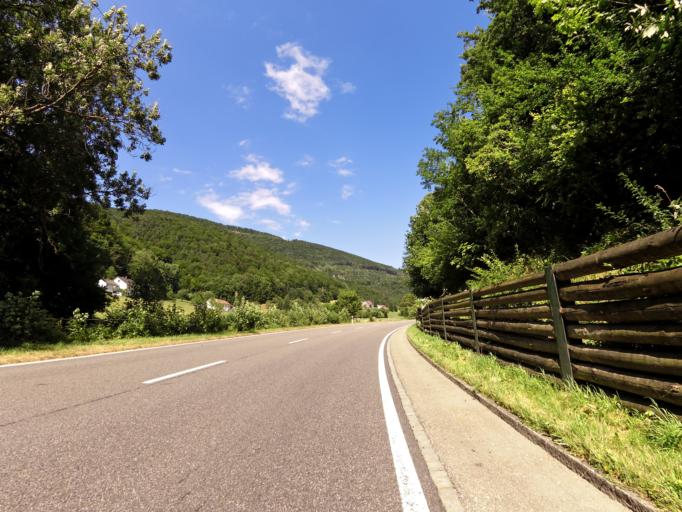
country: CH
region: Solothurn
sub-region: Bezirk Gaeu
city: Oberbuchsiten
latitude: 47.3292
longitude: 7.7373
